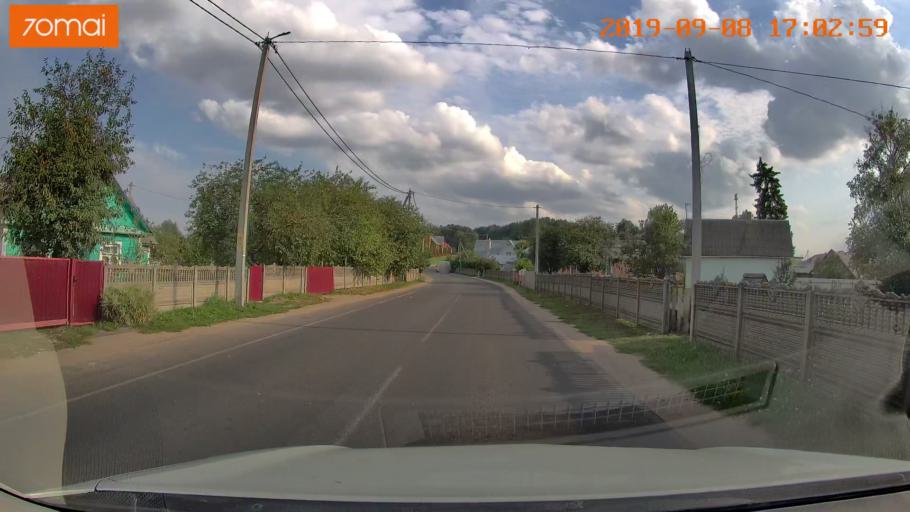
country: BY
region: Grodnenskaya
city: Hrodna
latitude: 53.6985
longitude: 23.9412
